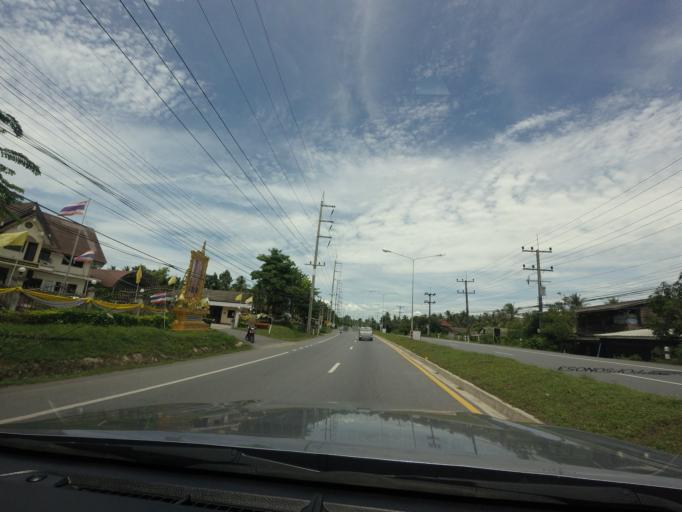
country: TH
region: Songkhla
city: Krasae Sin
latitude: 7.5987
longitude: 100.4020
